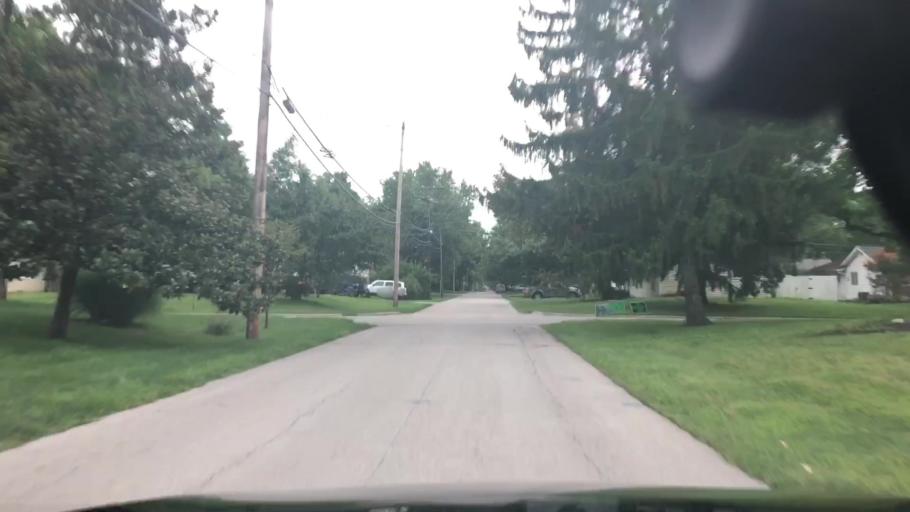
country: US
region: Ohio
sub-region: Franklin County
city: Upper Arlington
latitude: 40.0290
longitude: -83.0766
